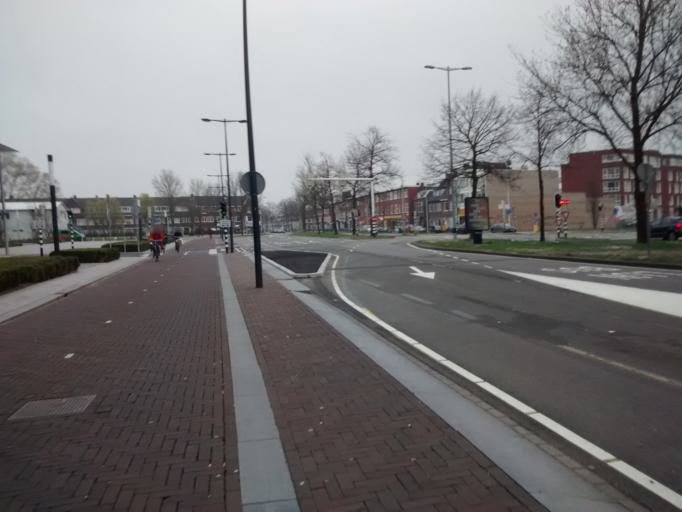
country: NL
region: Utrecht
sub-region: Gemeente Utrecht
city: Utrecht
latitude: 52.0855
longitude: 5.1087
